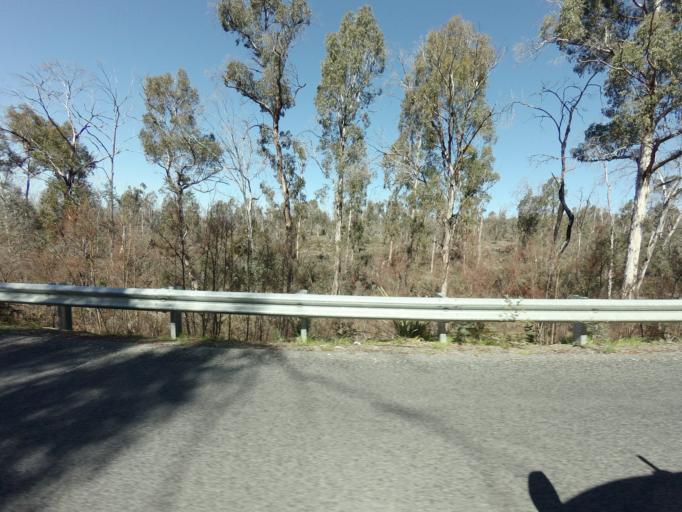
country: AU
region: Tasmania
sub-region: Derwent Valley
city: New Norfolk
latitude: -42.5433
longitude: 146.7180
